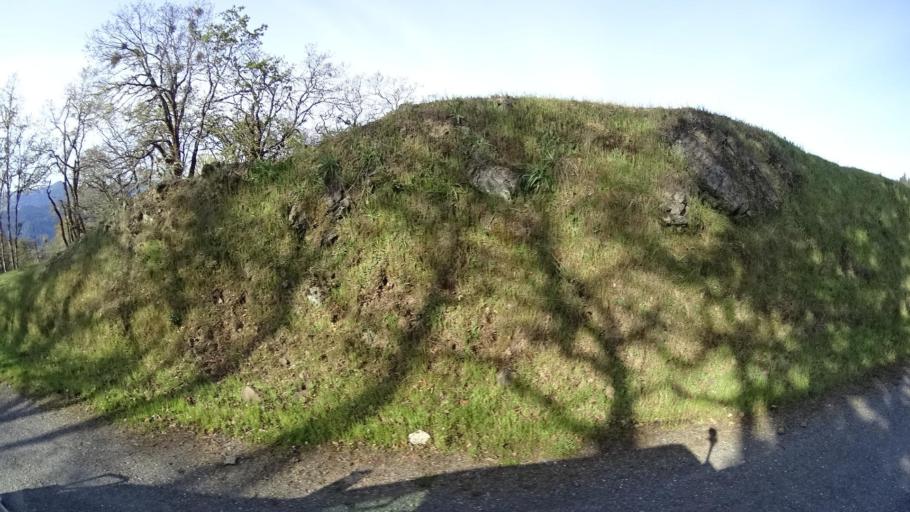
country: US
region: California
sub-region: Humboldt County
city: Hydesville
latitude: 40.6411
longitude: -123.9047
